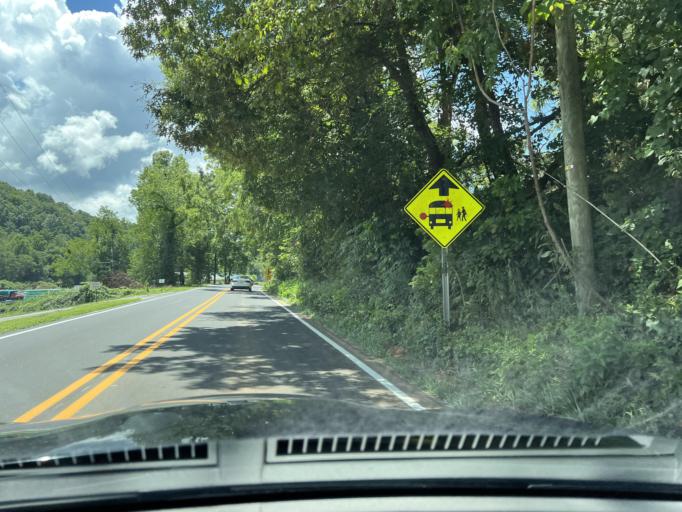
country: US
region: North Carolina
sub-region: Buncombe County
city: Fairview
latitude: 35.5127
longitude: -82.4100
